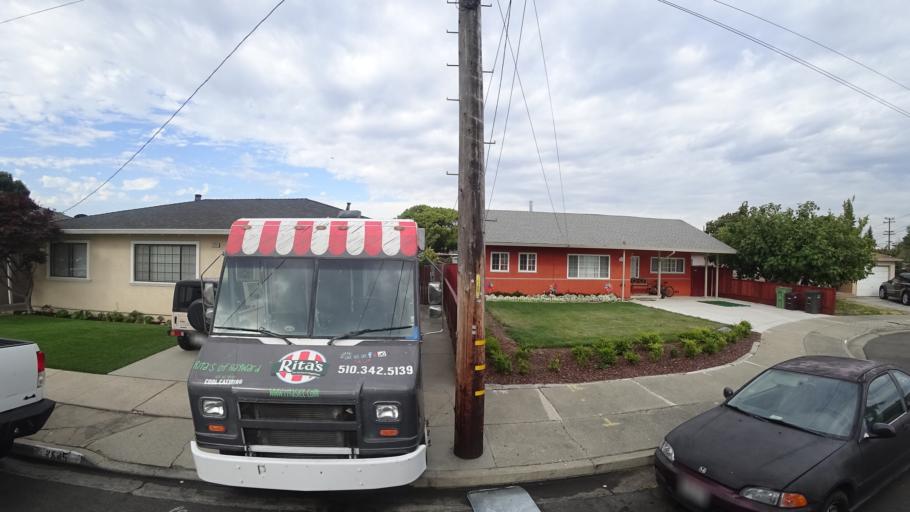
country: US
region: California
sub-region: Alameda County
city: Hayward
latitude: 37.6520
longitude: -122.0749
